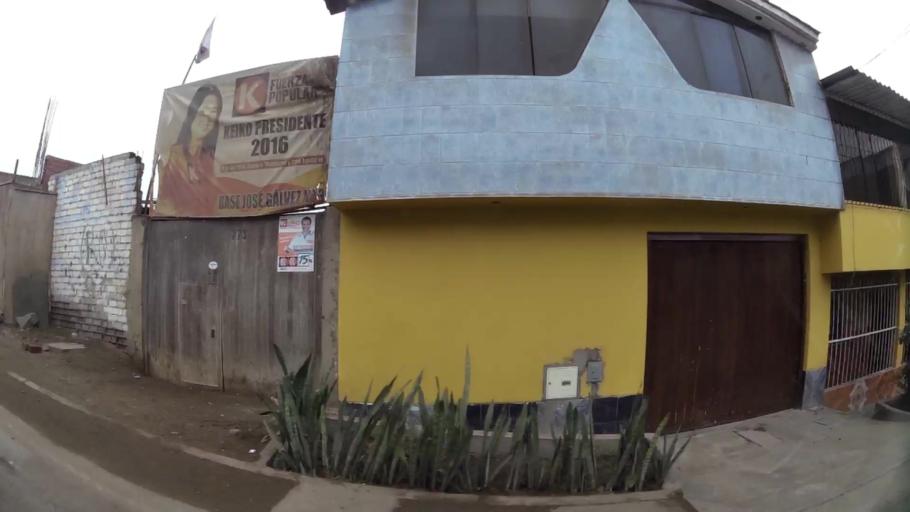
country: PE
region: Lima
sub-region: Lima
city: Surco
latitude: -12.2113
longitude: -76.9126
